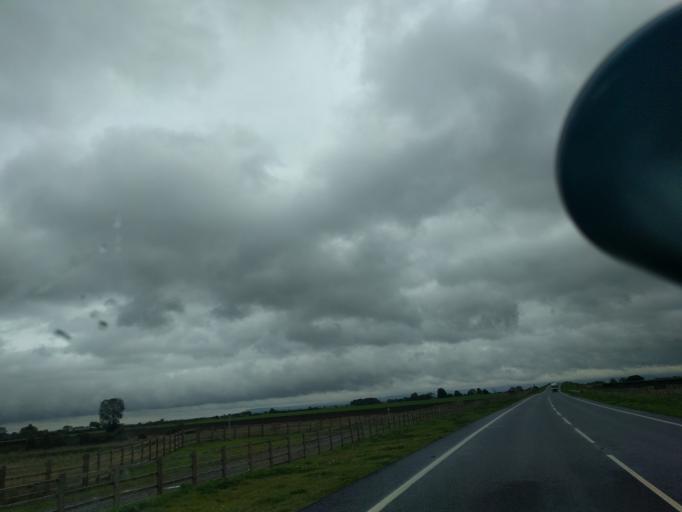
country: GB
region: England
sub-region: North Yorkshire
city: Bedale
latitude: 54.3129
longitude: -1.5584
